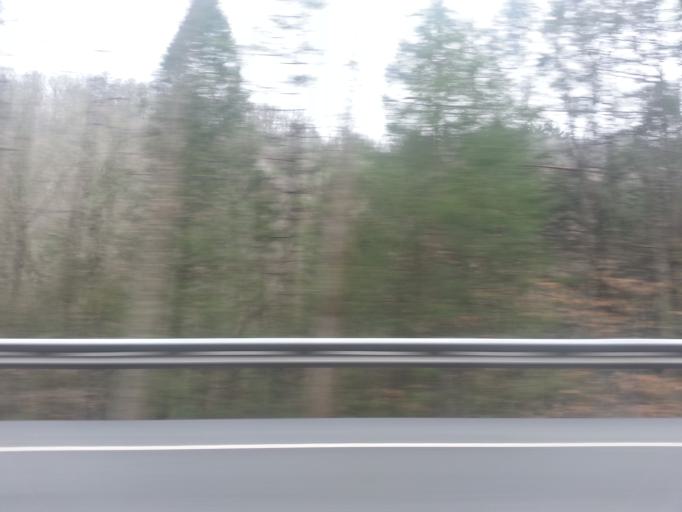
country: US
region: Tennessee
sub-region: Morgan County
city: Wartburg
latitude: 36.0359
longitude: -84.5254
